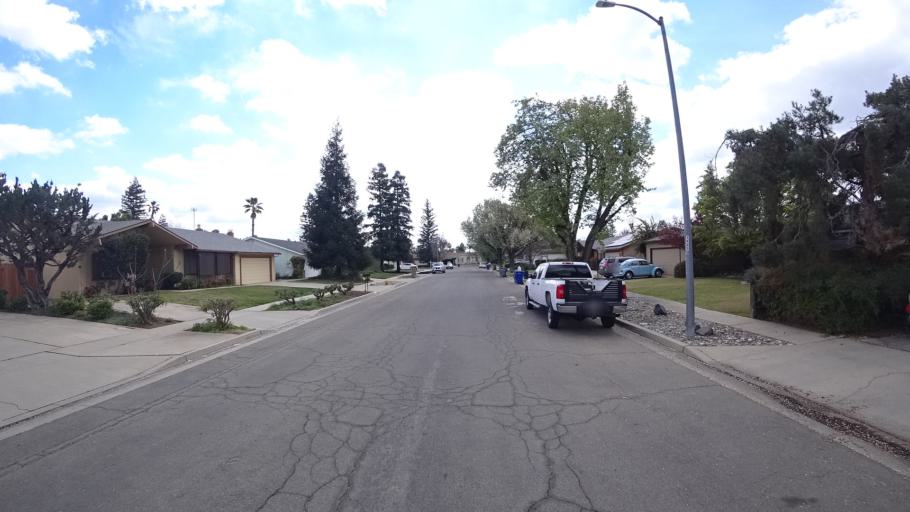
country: US
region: California
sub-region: Fresno County
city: Fresno
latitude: 36.8261
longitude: -119.8483
